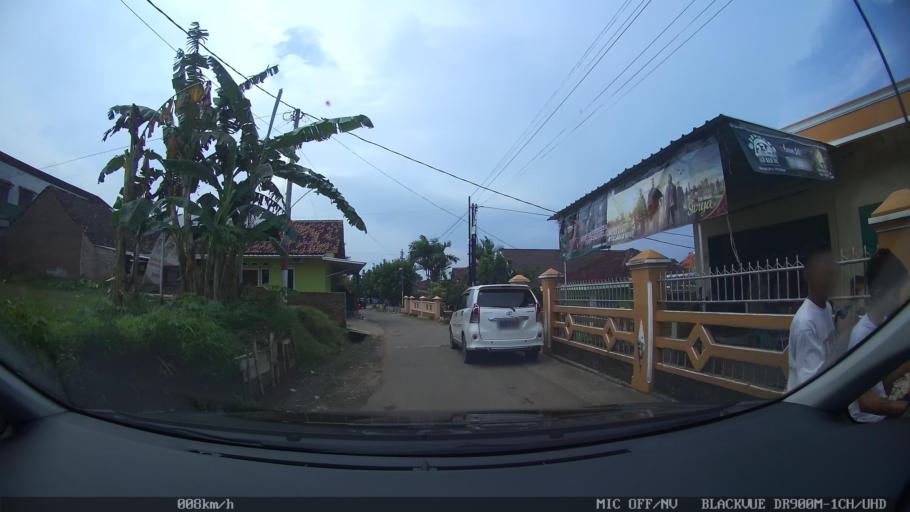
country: ID
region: Lampung
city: Kedaton
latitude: -5.3891
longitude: 105.2124
